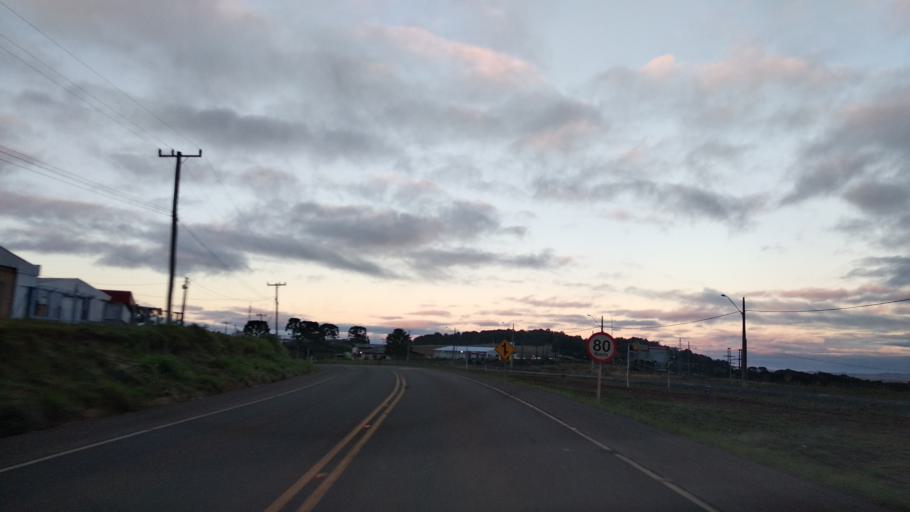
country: BR
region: Santa Catarina
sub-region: Campos Novos
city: Campos Novos
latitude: -27.3782
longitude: -51.2078
